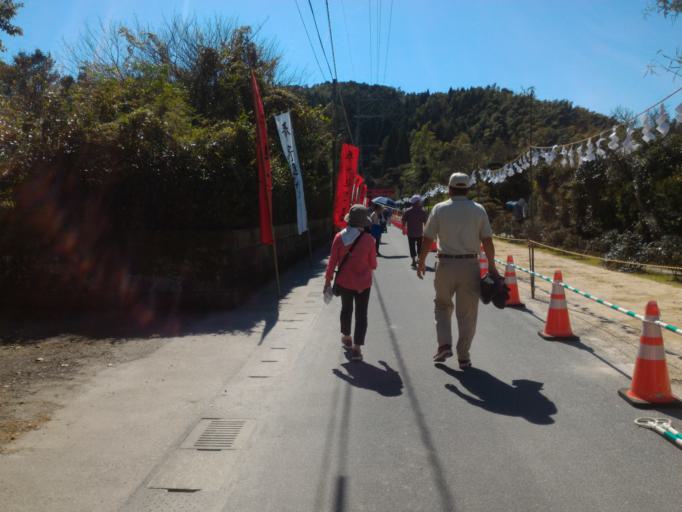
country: JP
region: Kagoshima
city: Kanoya
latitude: 31.3452
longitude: 130.9472
